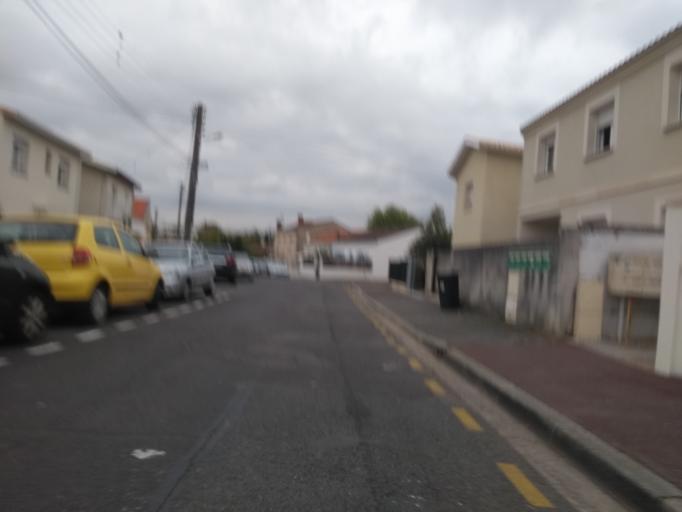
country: FR
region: Aquitaine
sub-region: Departement de la Gironde
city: Talence
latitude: 44.8056
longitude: -0.5952
